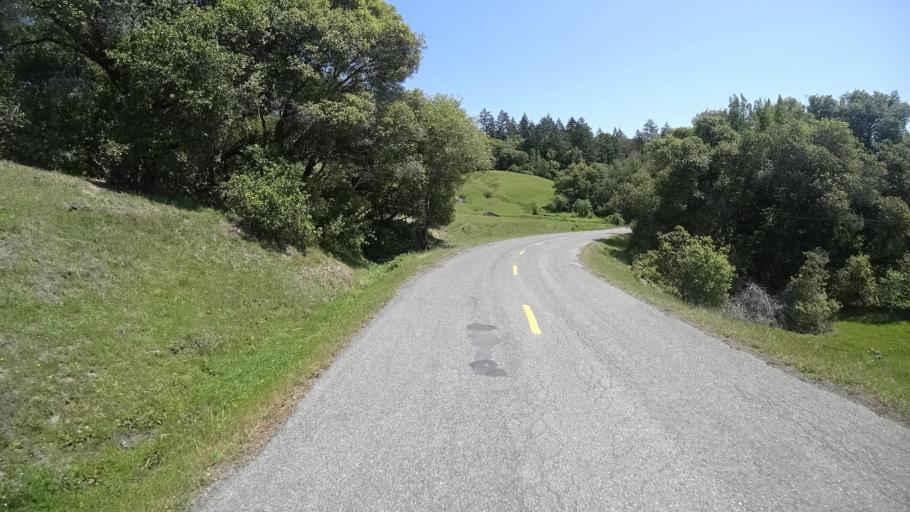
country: US
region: California
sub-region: Humboldt County
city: Redway
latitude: 40.2355
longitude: -123.6193
